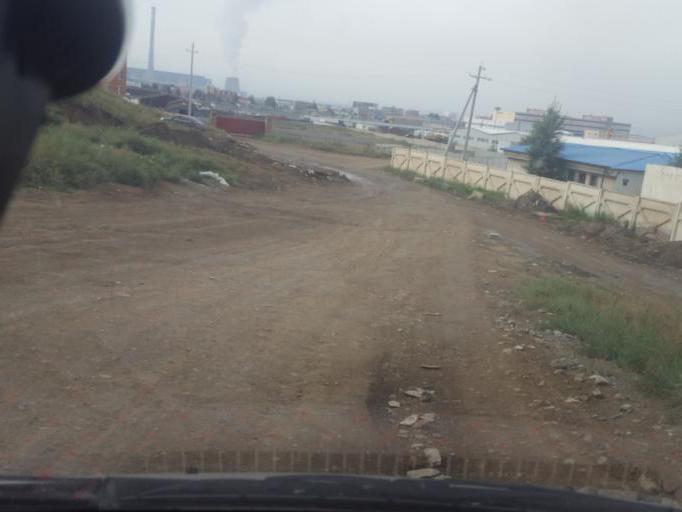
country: MN
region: Ulaanbaatar
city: Ulaanbaatar
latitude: 47.9160
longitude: 106.8006
